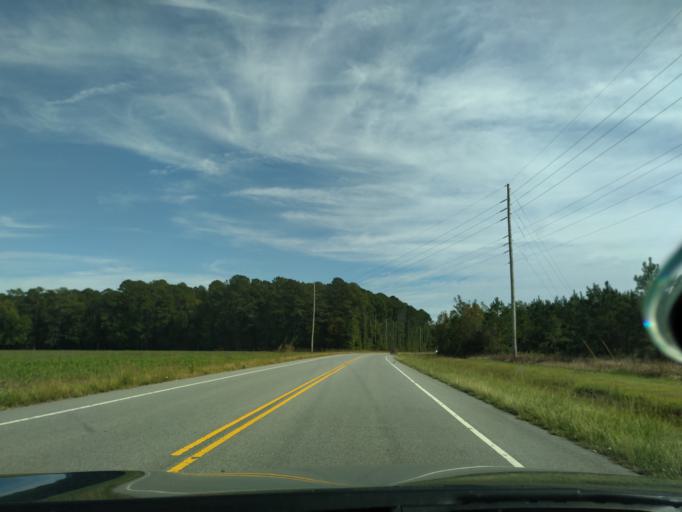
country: US
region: North Carolina
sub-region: Beaufort County
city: River Road
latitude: 35.5212
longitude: -76.9294
